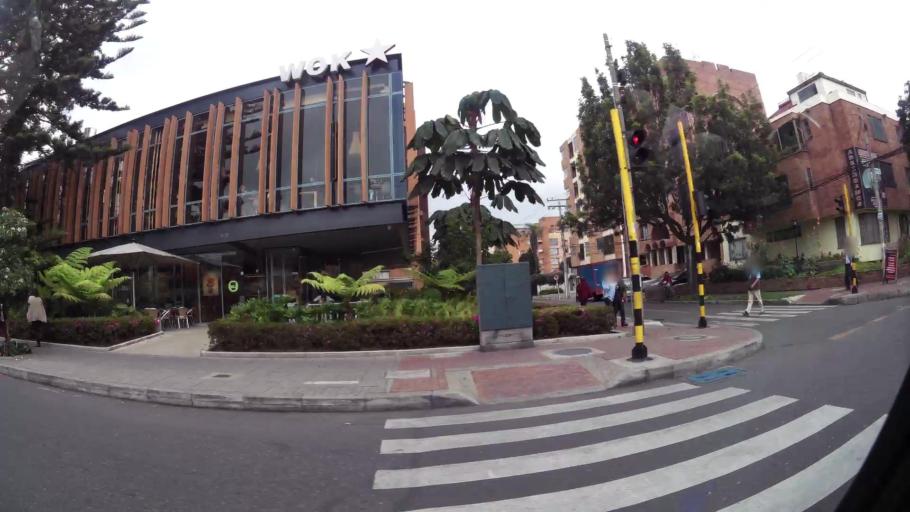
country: CO
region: Bogota D.C.
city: Barrio San Luis
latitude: 4.7197
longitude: -74.0375
